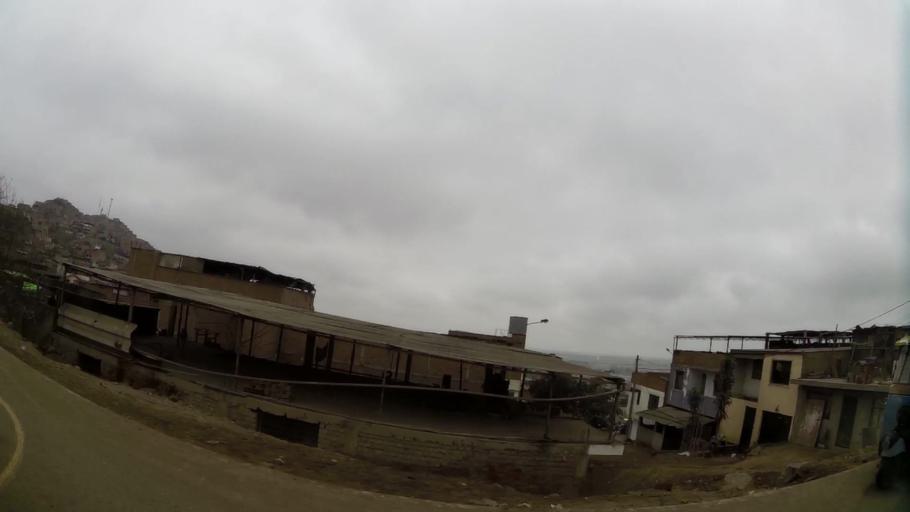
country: PE
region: Lima
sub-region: Lima
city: Surco
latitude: -12.1710
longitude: -76.9556
